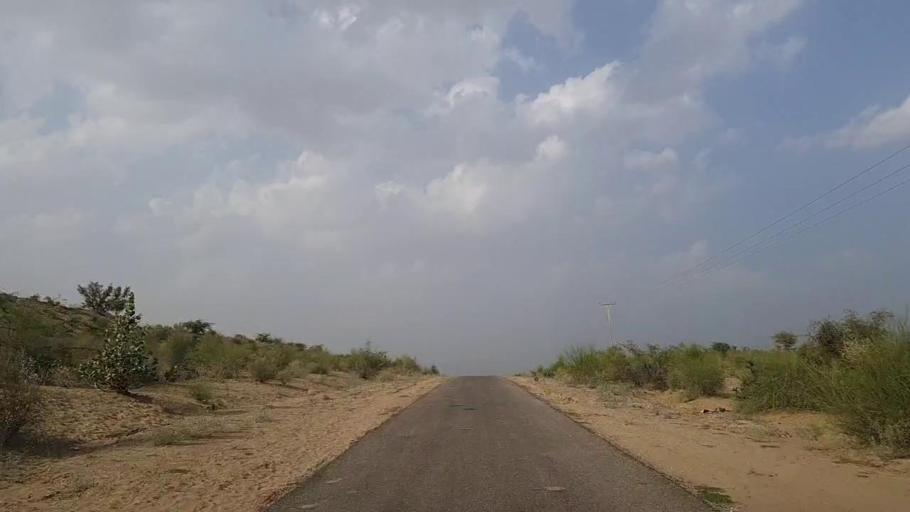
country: PK
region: Sindh
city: Islamkot
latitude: 24.7890
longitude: 70.2009
